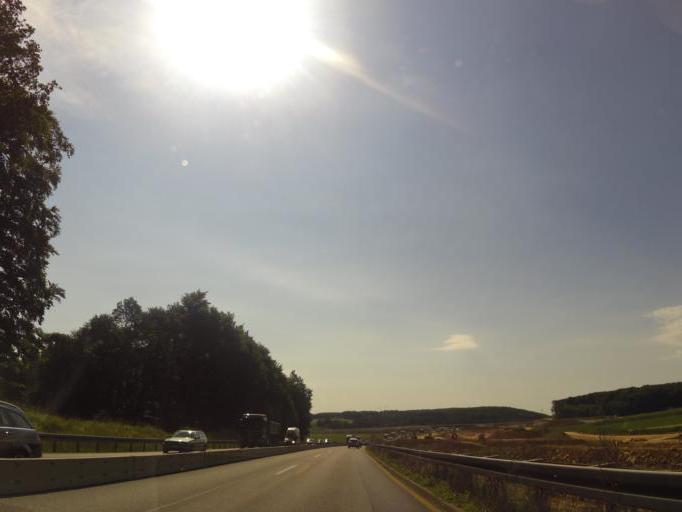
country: DE
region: Baden-Wuerttemberg
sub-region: Tuebingen Region
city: Nellingen
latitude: 48.5131
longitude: 9.8305
